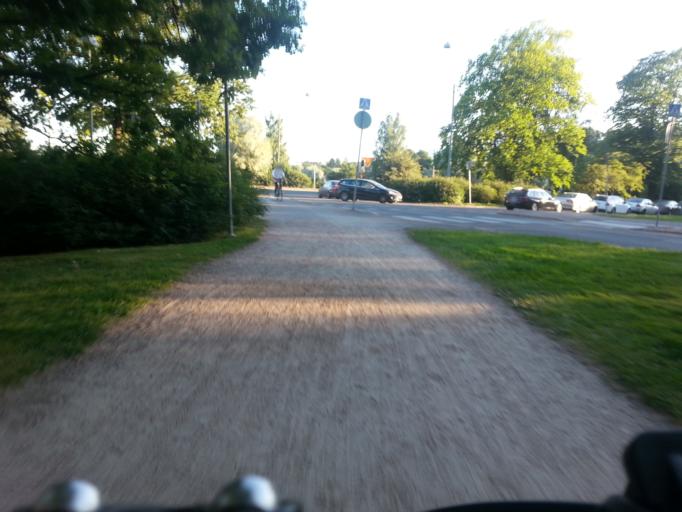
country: FI
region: Uusimaa
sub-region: Helsinki
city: Helsinki
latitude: 60.1856
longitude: 24.9341
